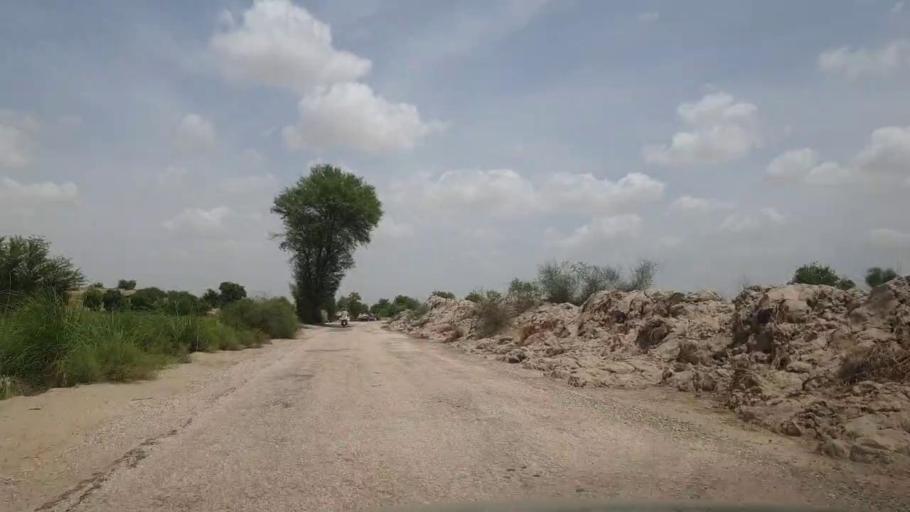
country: PK
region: Sindh
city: Kot Diji
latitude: 27.2165
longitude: 69.1076
